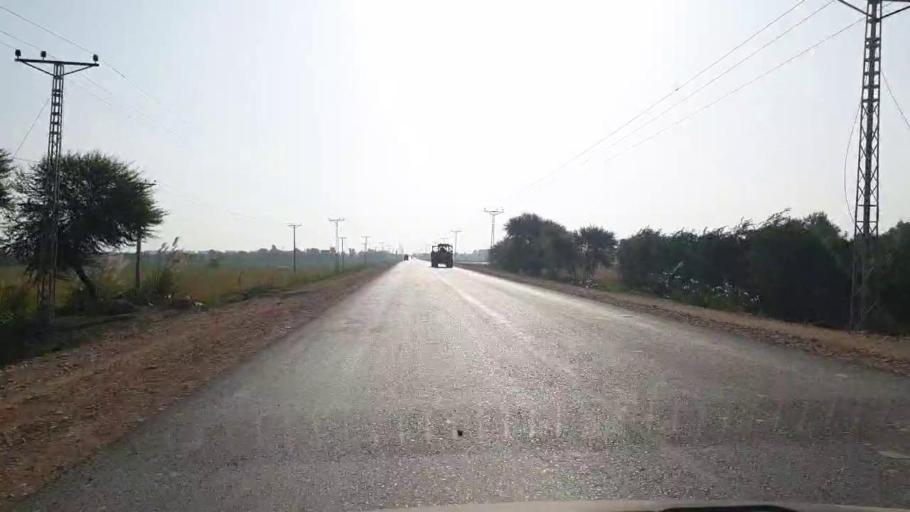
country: PK
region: Sindh
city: Badin
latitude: 24.6705
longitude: 68.8597
